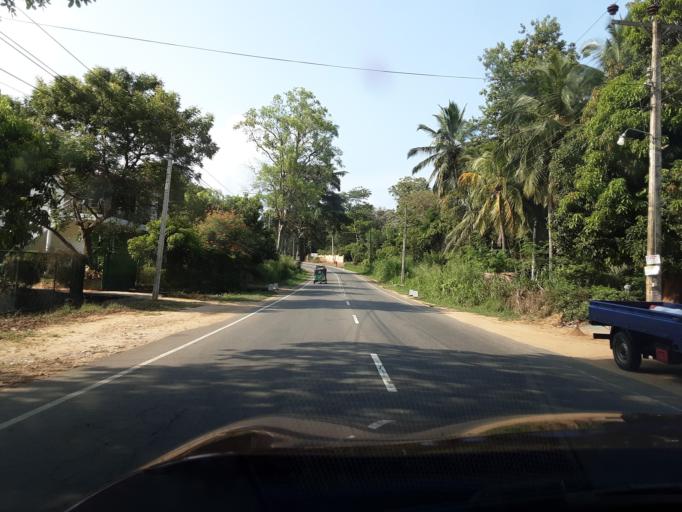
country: LK
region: Uva
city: Haputale
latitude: 6.5947
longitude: 81.1422
